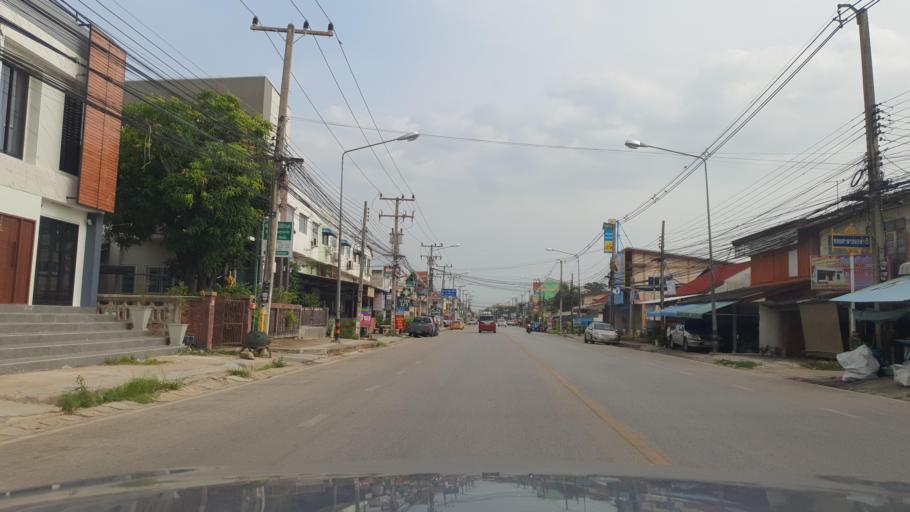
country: TH
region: Phitsanulok
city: Phitsanulok
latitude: 16.8527
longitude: 100.2544
